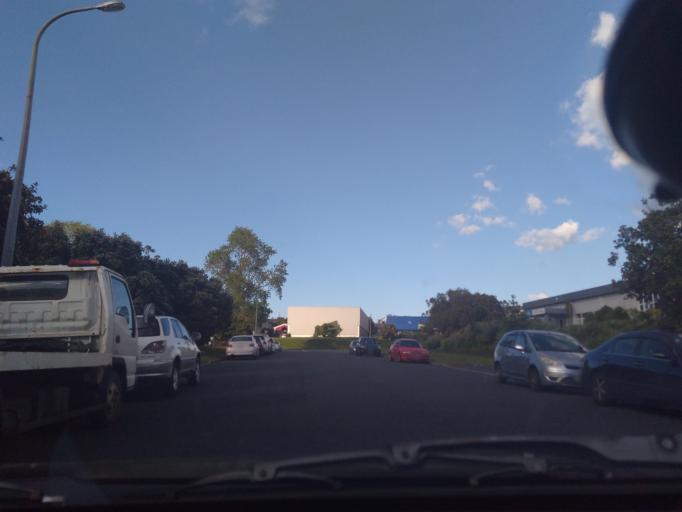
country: NZ
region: Auckland
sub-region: Auckland
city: Manukau City
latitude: -36.9419
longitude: 174.8867
